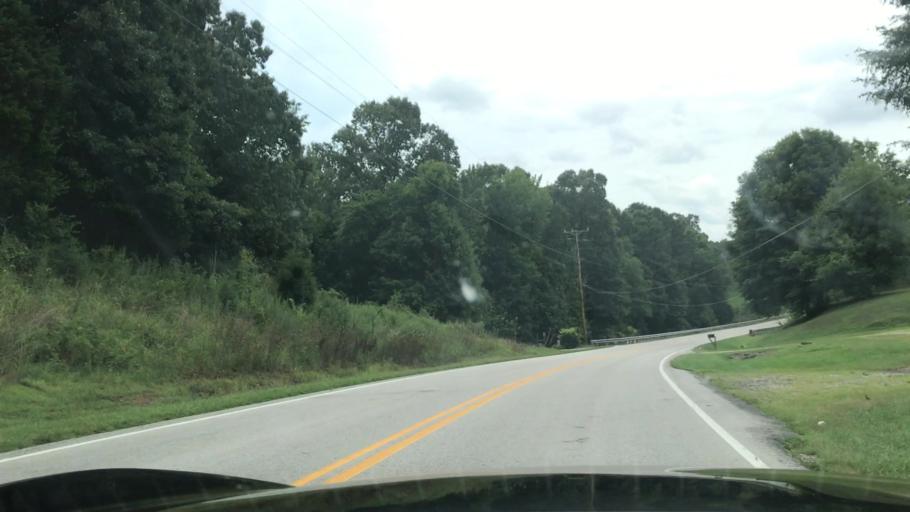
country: US
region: Kentucky
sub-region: Ohio County
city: Oak Grove
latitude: 37.2055
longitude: -86.8886
